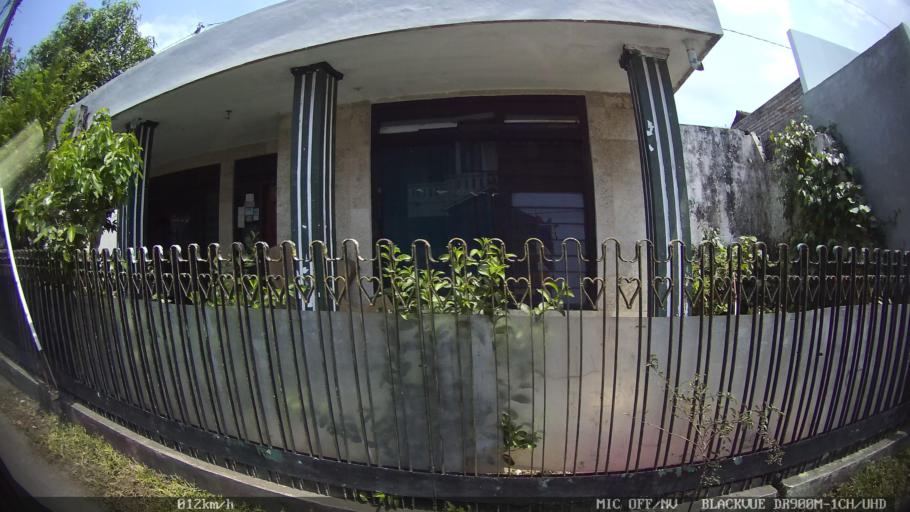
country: ID
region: Daerah Istimewa Yogyakarta
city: Yogyakarta
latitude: -7.8058
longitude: 110.4001
